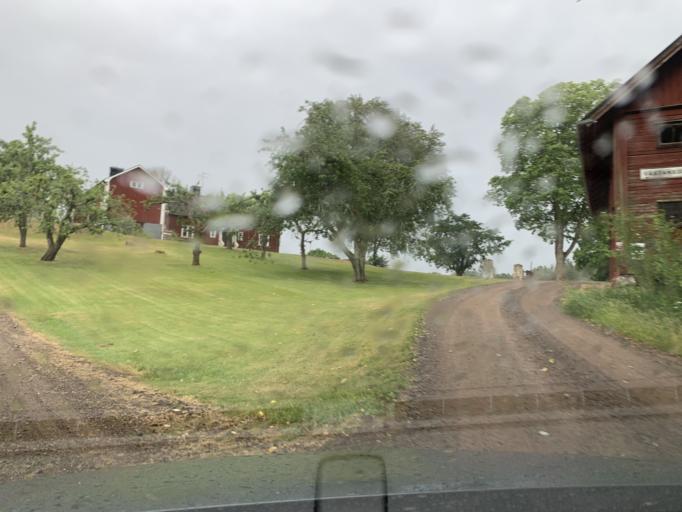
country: SE
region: Kalmar
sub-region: Vasterviks Kommun
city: Overum
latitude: 57.9927
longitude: 16.1778
